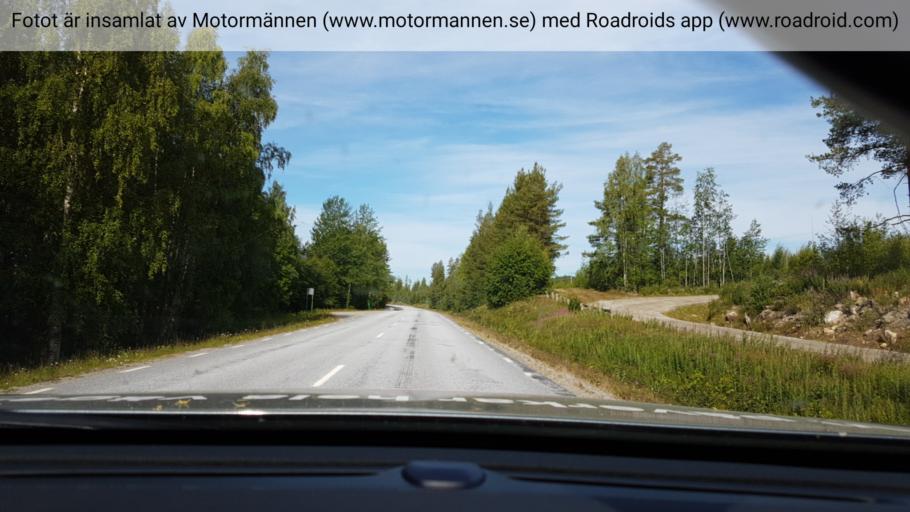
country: SE
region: Vaesterbotten
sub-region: Asele Kommun
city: Asele
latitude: 64.1881
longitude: 17.1694
